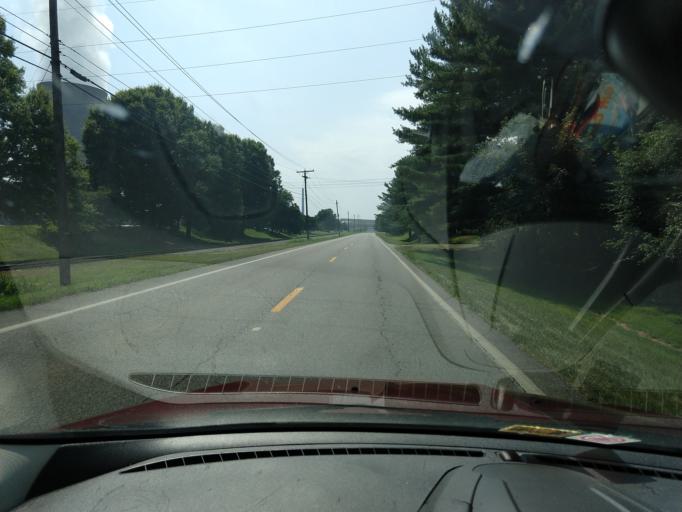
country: US
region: West Virginia
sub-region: Mason County
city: New Haven
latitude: 38.9788
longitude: -81.9434
